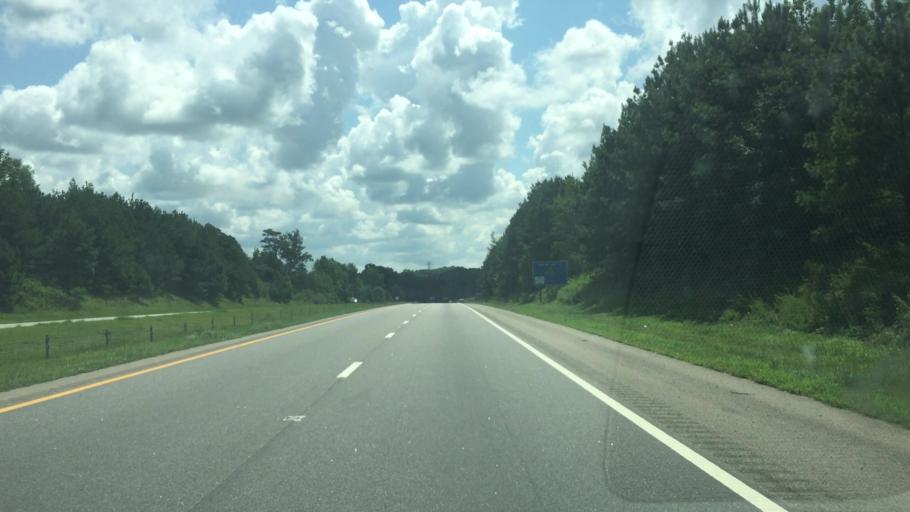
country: US
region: North Carolina
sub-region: Richmond County
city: Cordova
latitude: 34.9197
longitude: -79.8086
